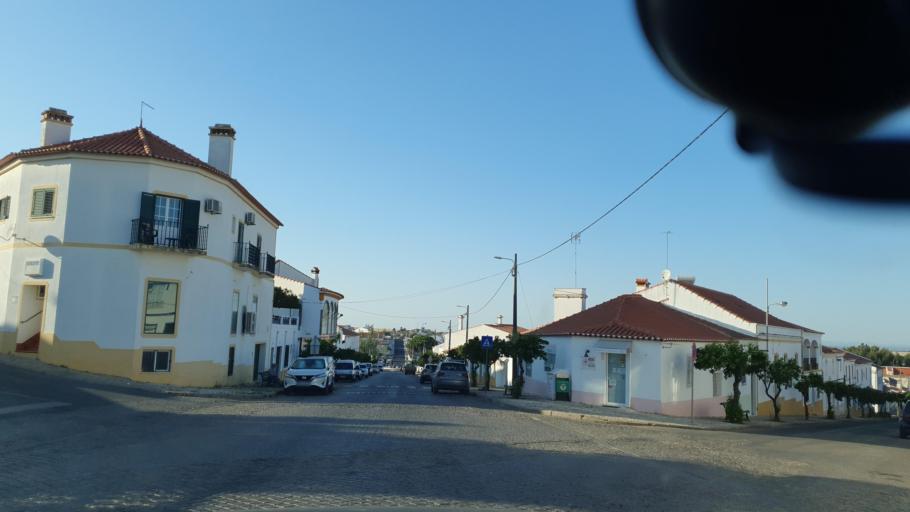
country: PT
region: Portalegre
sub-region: Fronteira
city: Fronteira
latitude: 38.9550
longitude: -7.6745
